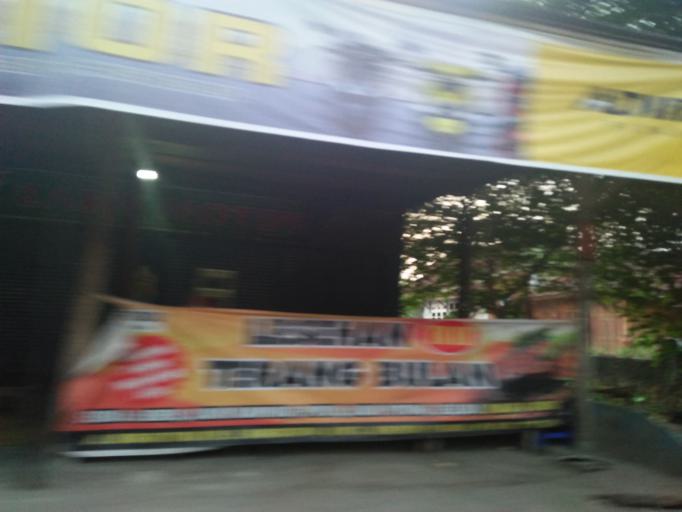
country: ID
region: Daerah Istimewa Yogyakarta
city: Sewon
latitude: -7.8392
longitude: 110.3916
